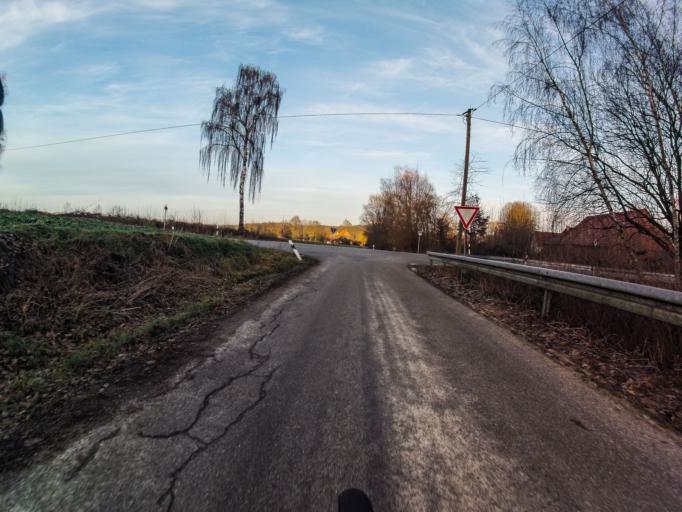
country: DE
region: North Rhine-Westphalia
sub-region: Regierungsbezirk Munster
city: Mettingen
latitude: 52.2993
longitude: 7.8073
